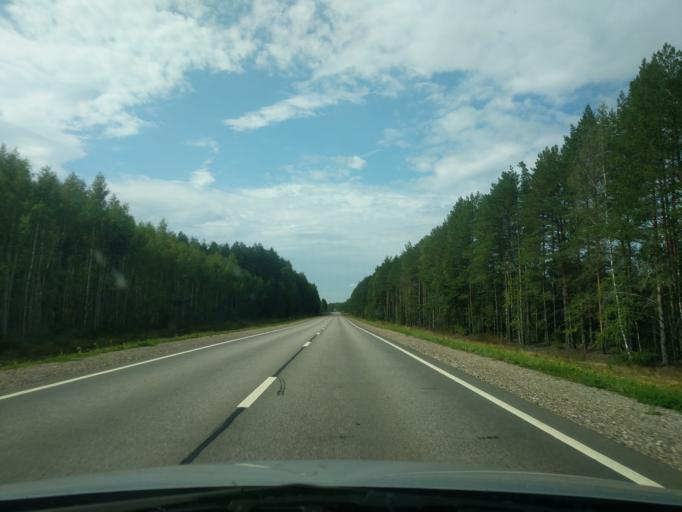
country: RU
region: Kostroma
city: Kadyy
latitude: 57.7972
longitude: 42.8950
